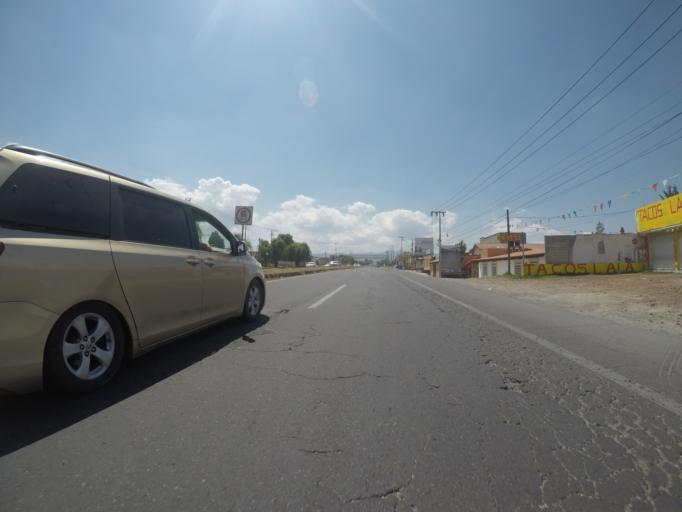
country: MX
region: Mexico
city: Santa Cruz Cuauhtenco
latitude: 19.2543
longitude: -99.7282
